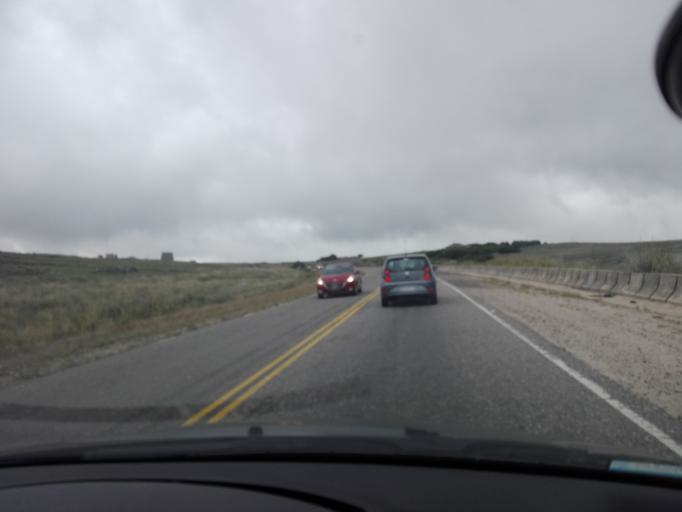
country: AR
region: Cordoba
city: Cuesta Blanca
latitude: -31.6091
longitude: -64.7536
